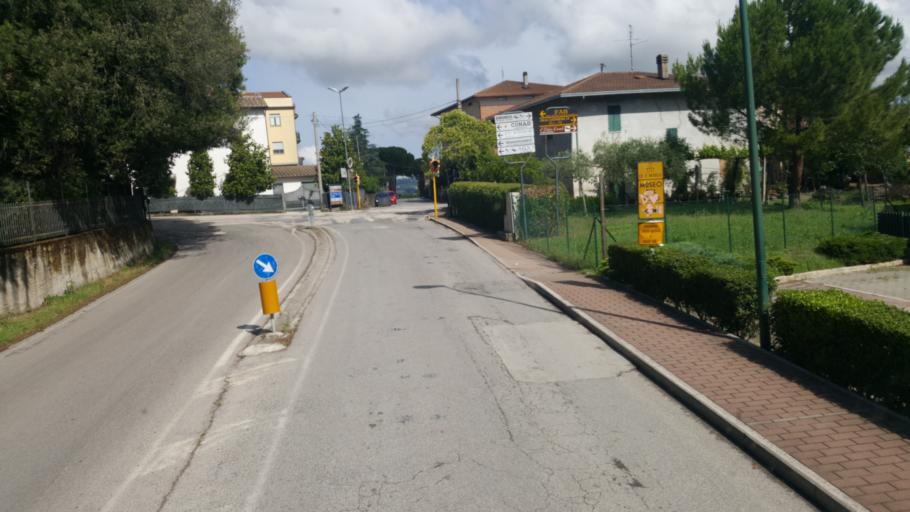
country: IT
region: Umbria
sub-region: Provincia di Perugia
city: Torgiano
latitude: 43.0287
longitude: 12.4413
